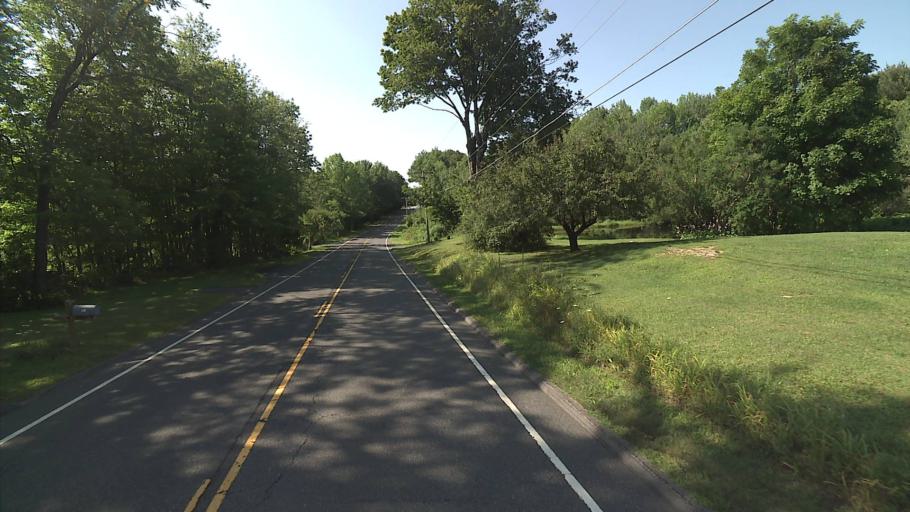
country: US
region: Massachusetts
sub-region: Hampden County
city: Granville
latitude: 42.0098
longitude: -72.9707
